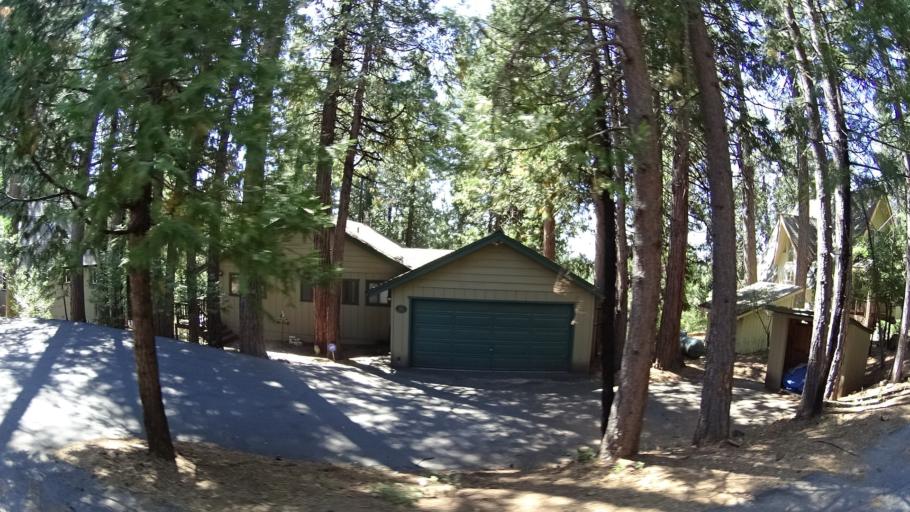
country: US
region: California
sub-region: Calaveras County
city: Arnold
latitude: 38.2403
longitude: -120.3338
